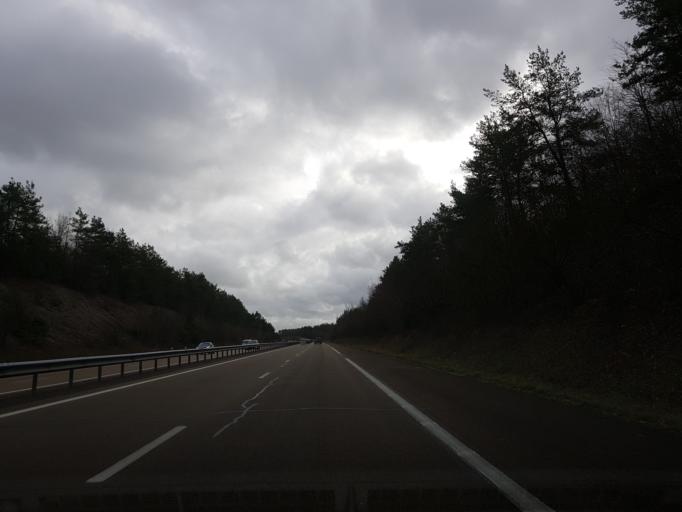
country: FR
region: Champagne-Ardenne
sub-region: Departement de la Haute-Marne
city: Chamarandes-Choignes
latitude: 48.0176
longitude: 5.0970
